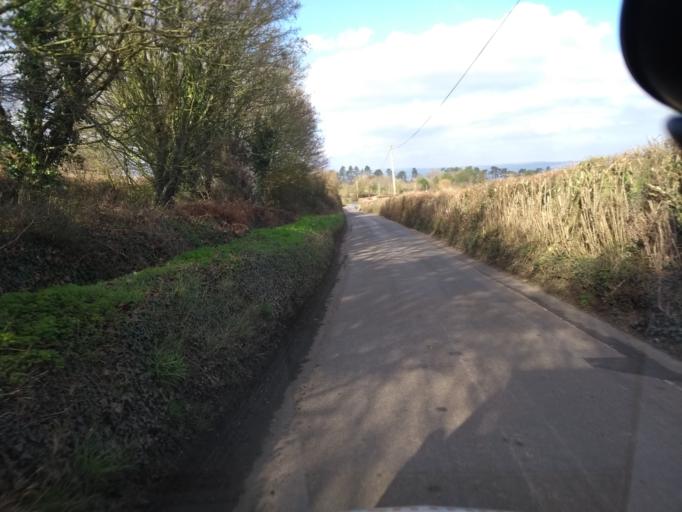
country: GB
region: England
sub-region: Somerset
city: Creech Saint Michael
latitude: 50.9737
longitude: -3.0544
